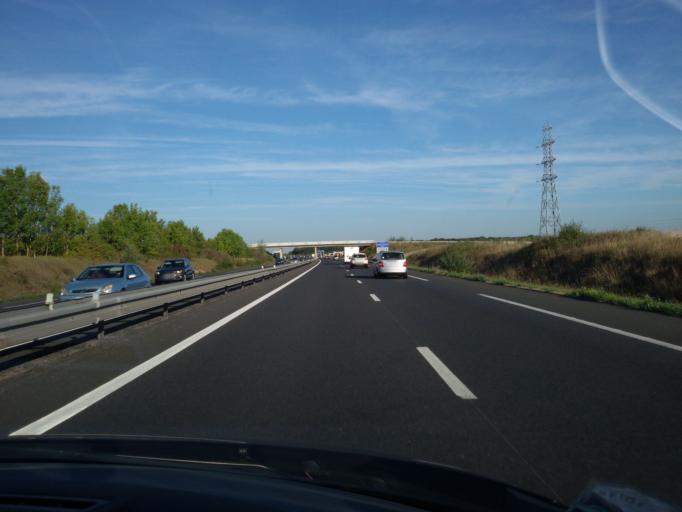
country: FR
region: Centre
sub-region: Departement du Cher
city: Marmagne
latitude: 47.0904
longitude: 2.2527
